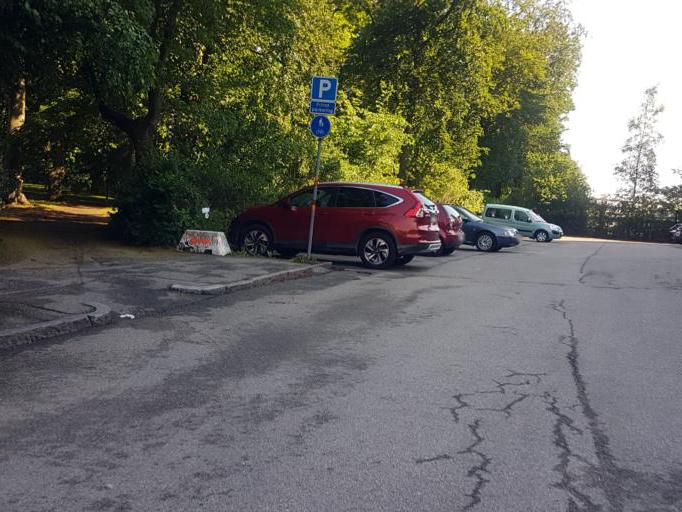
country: SE
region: Skane
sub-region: Lunds Kommun
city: Lund
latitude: 55.7059
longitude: 13.2114
